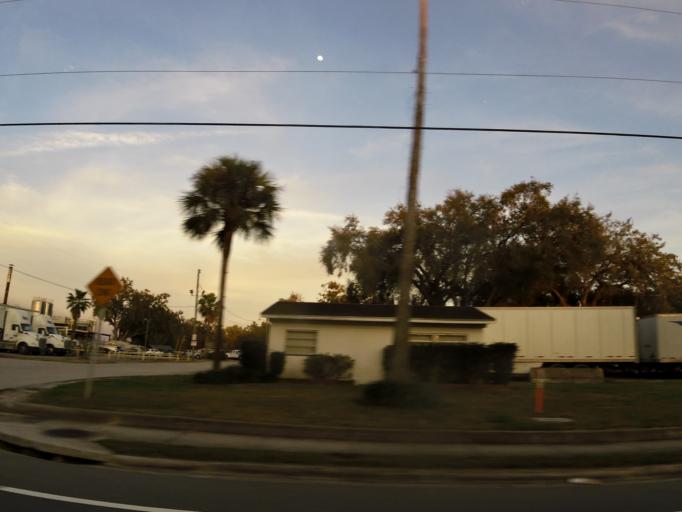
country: US
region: Florida
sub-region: Volusia County
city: North DeLand
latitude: 29.0671
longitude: -81.3045
